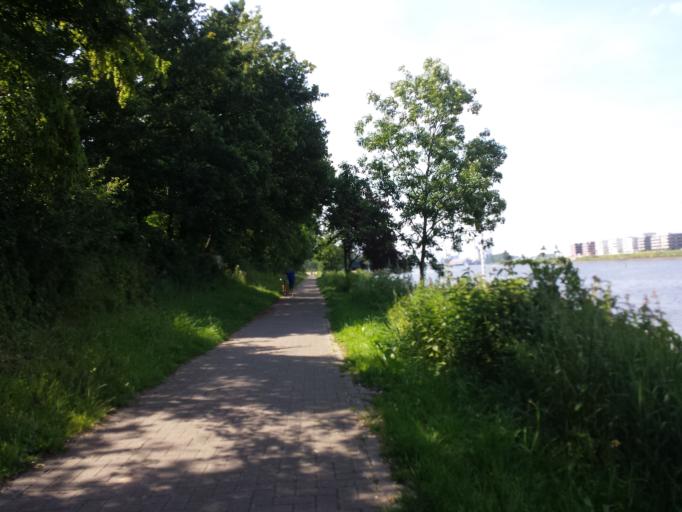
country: DE
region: Bremen
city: Bremen
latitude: 53.0950
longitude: 8.7575
